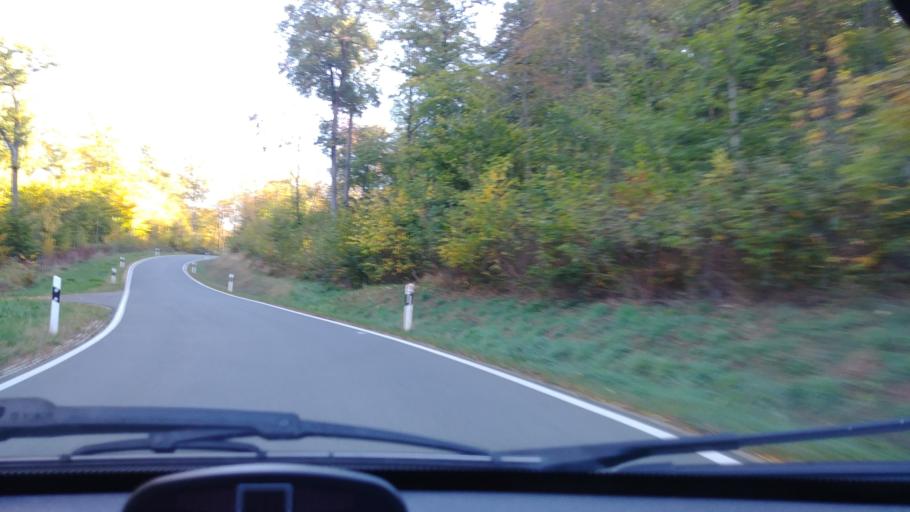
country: DE
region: Rheinland-Pfalz
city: Lollschied
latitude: 50.2566
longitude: 7.8805
